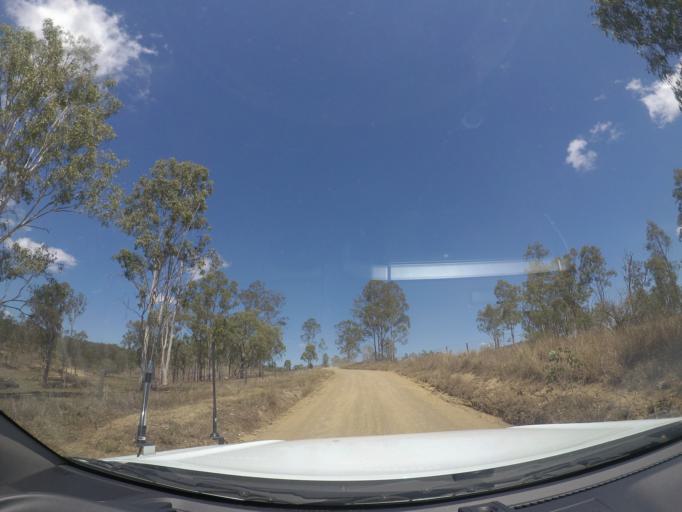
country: AU
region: Queensland
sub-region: Logan
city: Cedar Vale
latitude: -27.8570
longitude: 152.8805
